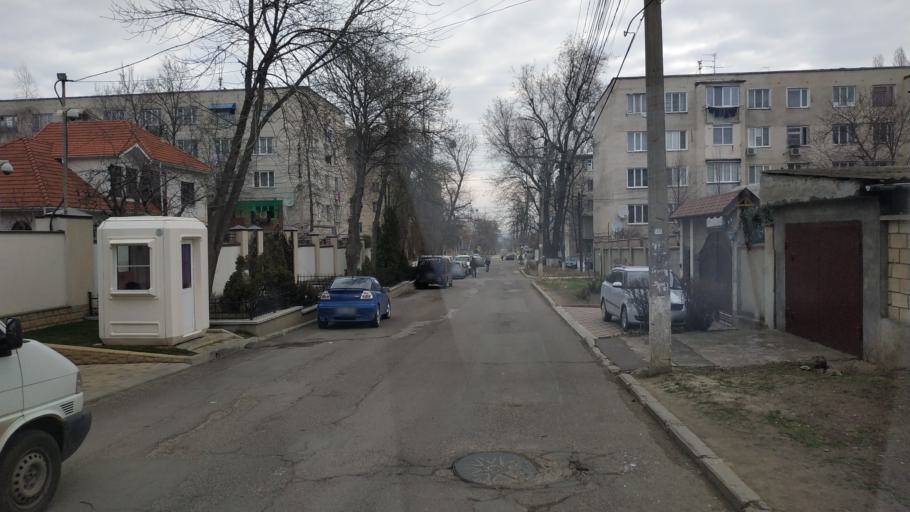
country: MD
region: Chisinau
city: Vatra
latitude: 47.0316
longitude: 28.7863
